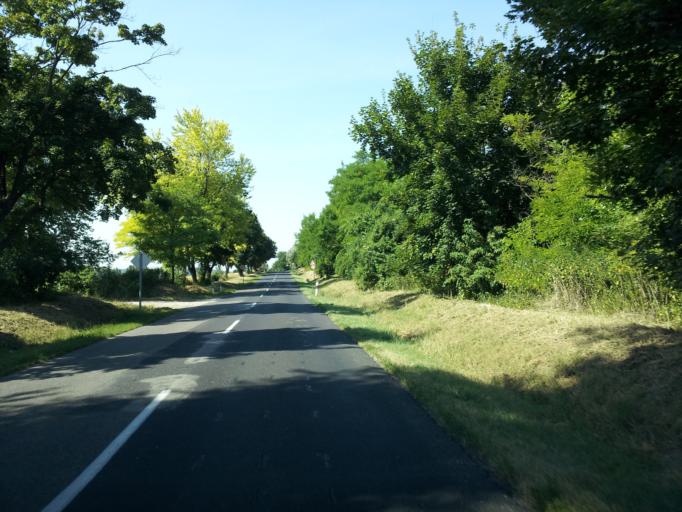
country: HU
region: Fejer
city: Lovasbereny
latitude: 47.3131
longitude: 18.5626
